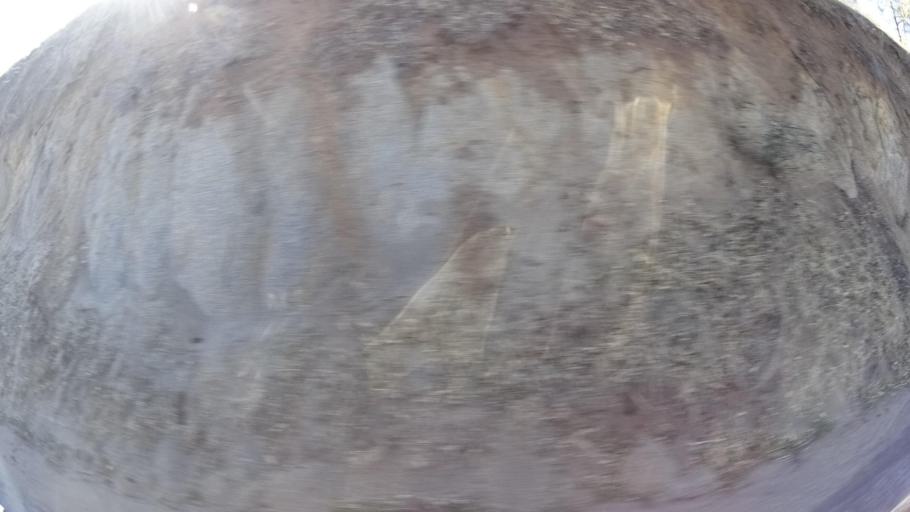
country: US
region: California
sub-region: Kern County
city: Bear Valley Springs
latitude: 35.3447
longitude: -118.5719
